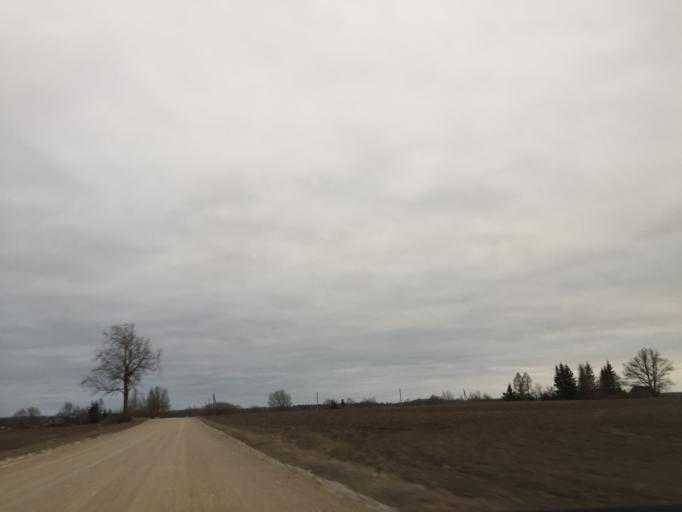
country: LT
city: Zagare
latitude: 56.2758
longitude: 23.2611
